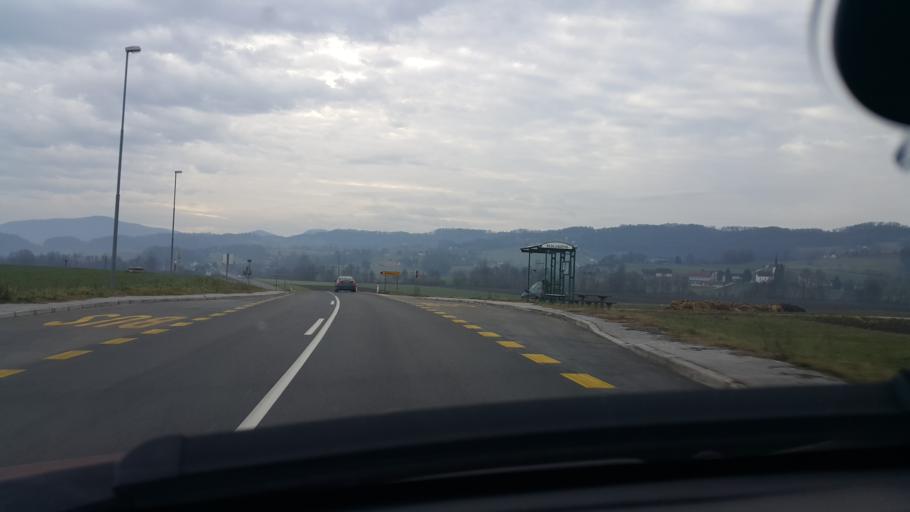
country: SI
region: Kozje
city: Kozje
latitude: 46.1000
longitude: 15.6113
